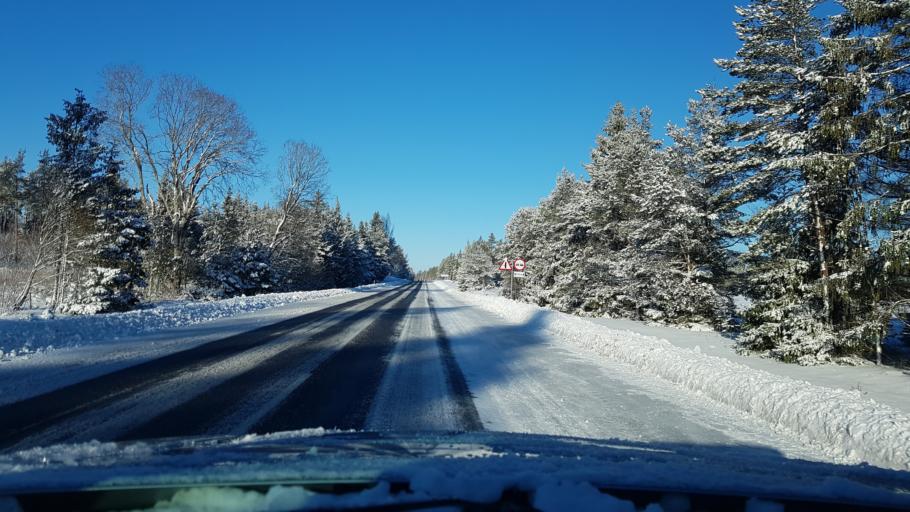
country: EE
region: Hiiumaa
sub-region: Kaerdla linn
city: Kardla
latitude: 58.9691
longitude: 22.8290
